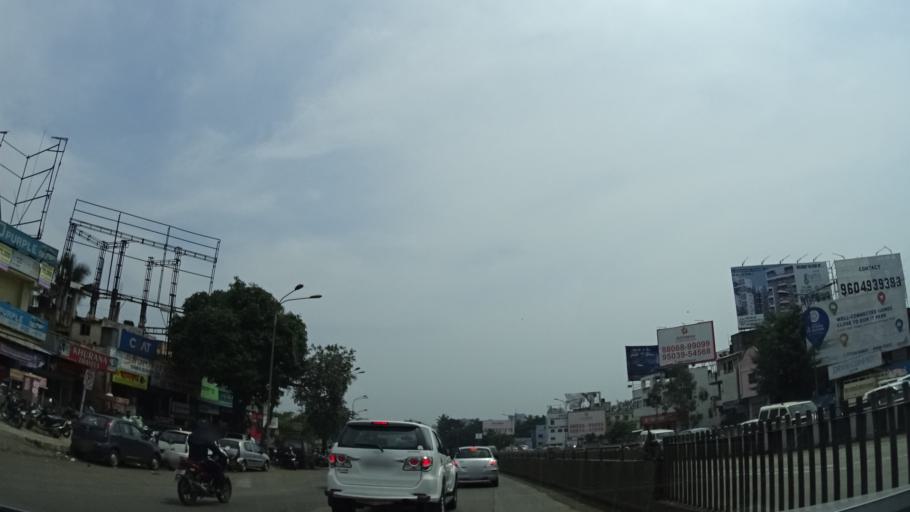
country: IN
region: Maharashtra
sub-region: Pune Division
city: Lohogaon
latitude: 18.5624
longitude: 73.9389
